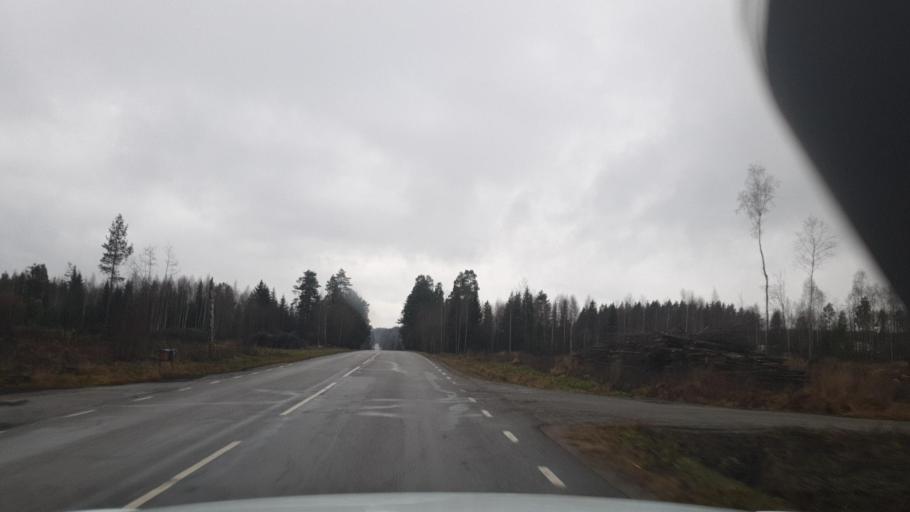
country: SE
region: Vaermland
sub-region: Arvika Kommun
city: Arvika
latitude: 59.6916
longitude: 12.6338
